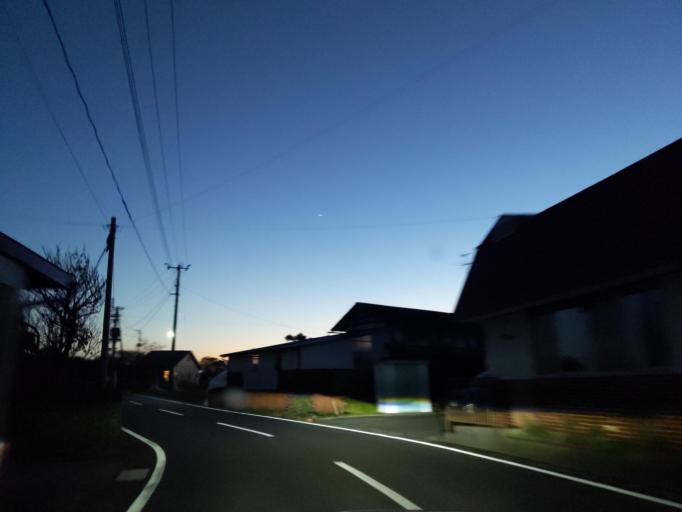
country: JP
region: Fukushima
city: Sukagawa
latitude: 37.3370
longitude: 140.3889
